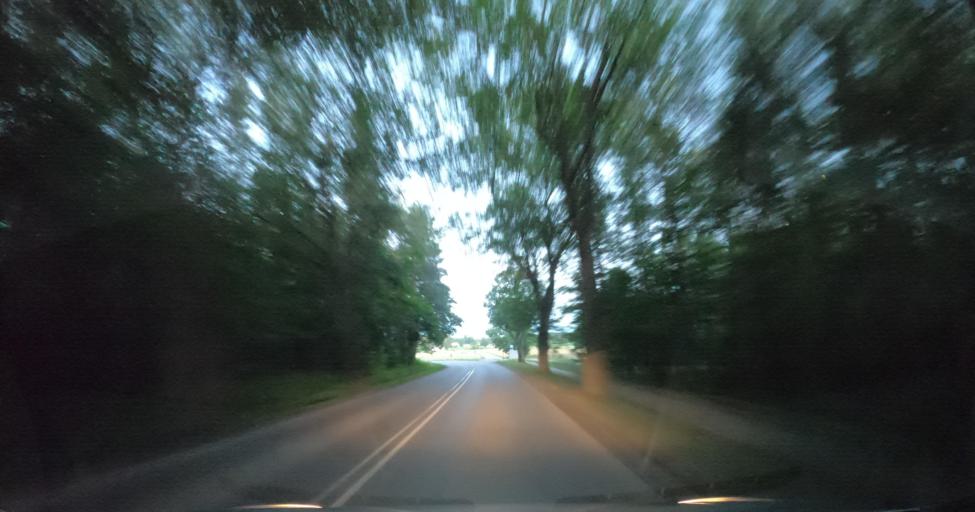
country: PL
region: Pomeranian Voivodeship
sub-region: Powiat wejherowski
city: Szemud
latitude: 54.4675
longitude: 18.2815
